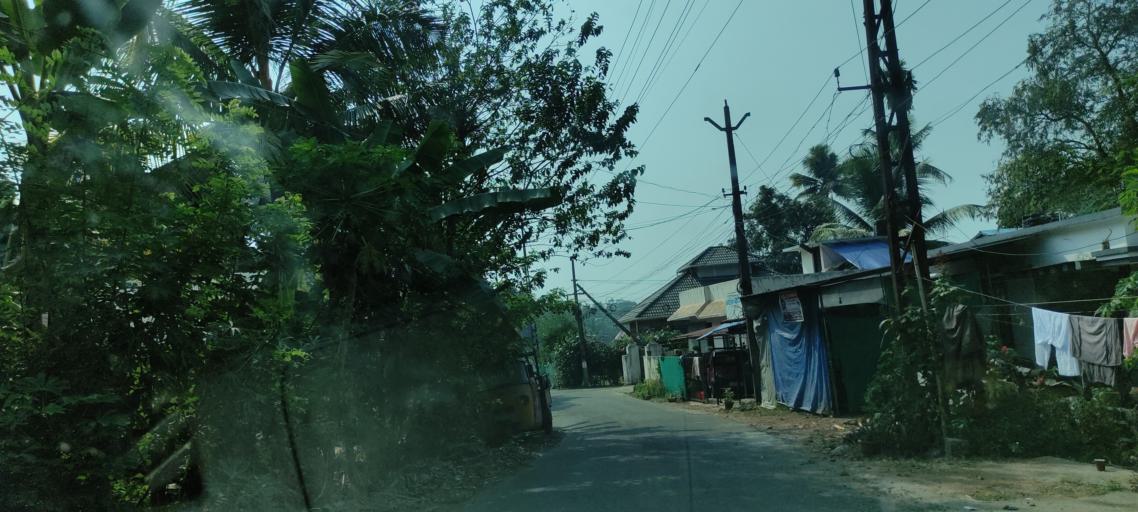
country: IN
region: Kerala
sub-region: Pattanamtitta
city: Tiruvalla
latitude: 9.3595
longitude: 76.5133
